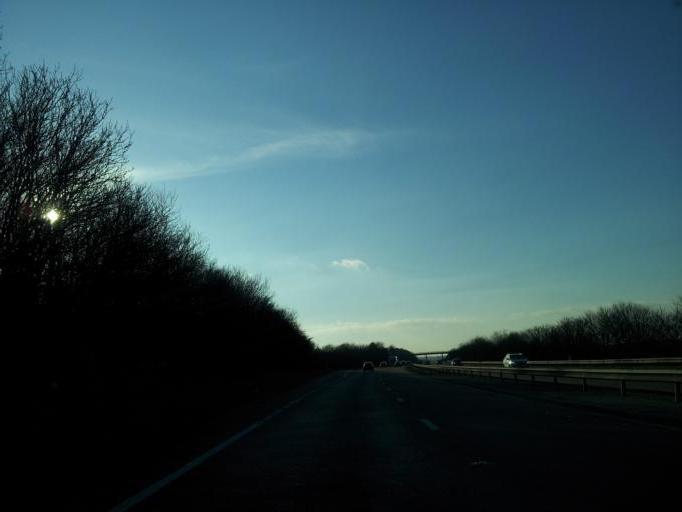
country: GB
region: England
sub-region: Devon
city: Okehampton
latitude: 50.7307
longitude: -3.8759
